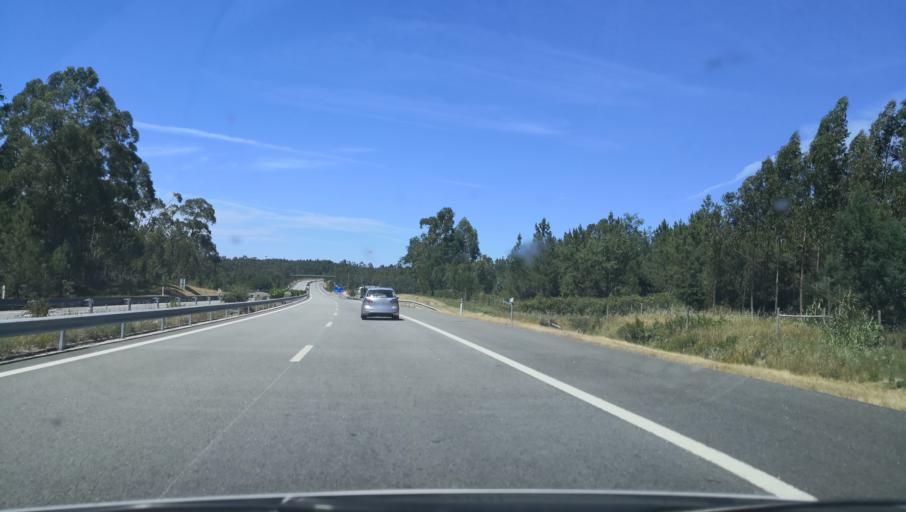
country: PT
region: Coimbra
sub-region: Montemor-O-Velho
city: Montemor-o-Velho
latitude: 40.2090
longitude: -8.6742
